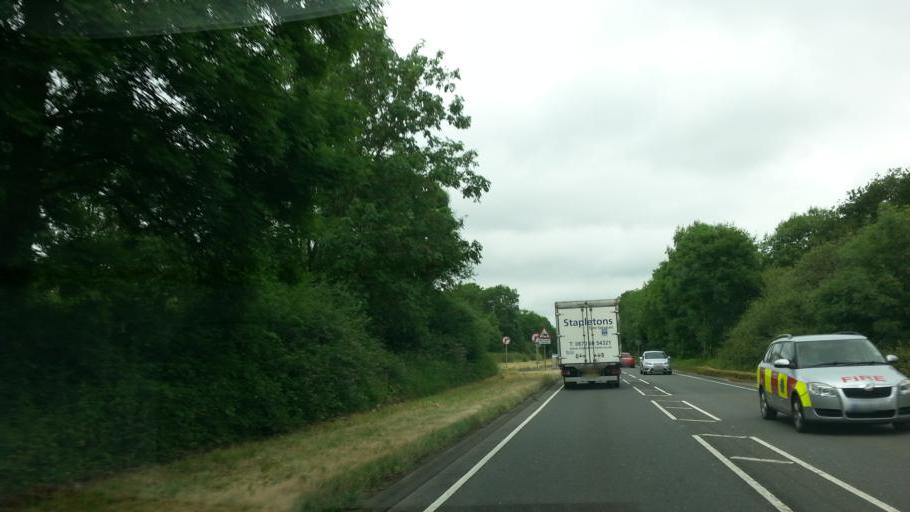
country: GB
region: England
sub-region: Northamptonshire
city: Broughton
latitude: 52.3275
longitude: -0.7904
